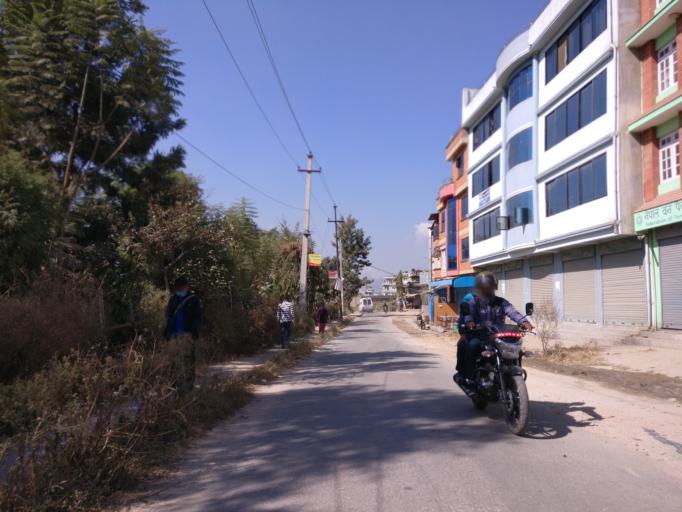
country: NP
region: Central Region
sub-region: Bagmati Zone
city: Patan
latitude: 27.6751
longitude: 85.3397
